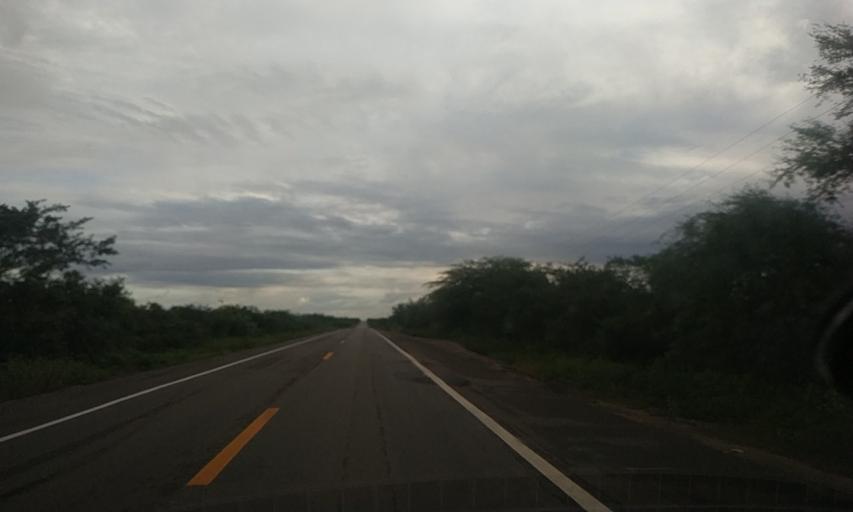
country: BR
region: Rio Grande do Norte
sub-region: Mossoro
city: Mossoro
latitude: -5.1380
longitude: -37.2118
